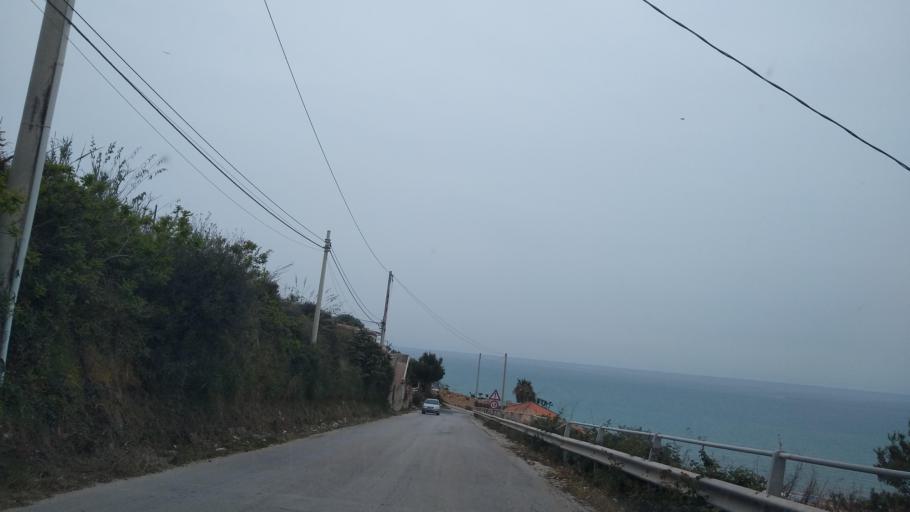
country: IT
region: Sicily
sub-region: Trapani
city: Castellammare del Golfo
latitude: 38.0211
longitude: 12.8974
